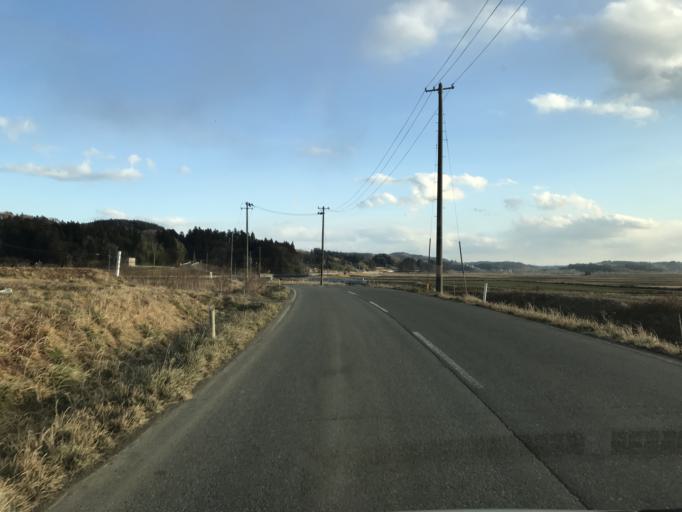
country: JP
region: Iwate
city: Ichinoseki
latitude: 38.9689
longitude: 141.1641
